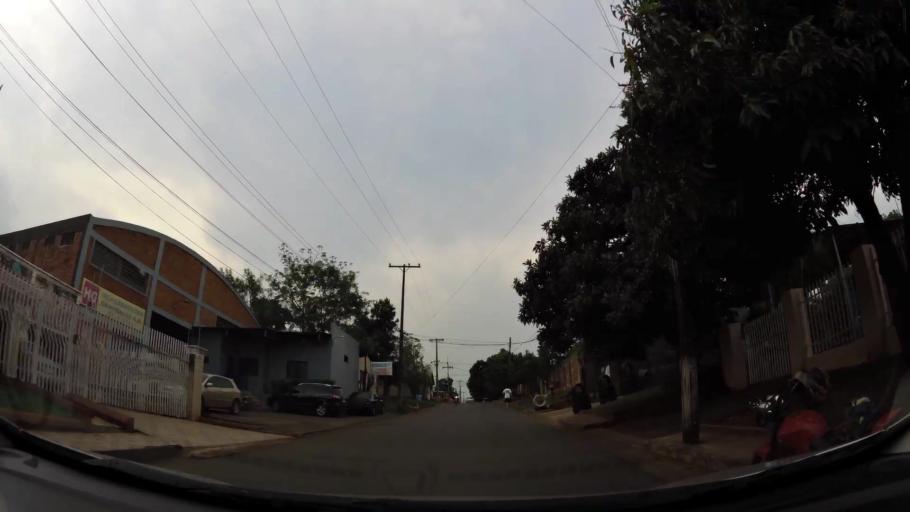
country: PY
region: Alto Parana
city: Presidente Franco
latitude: -25.5377
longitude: -54.6134
